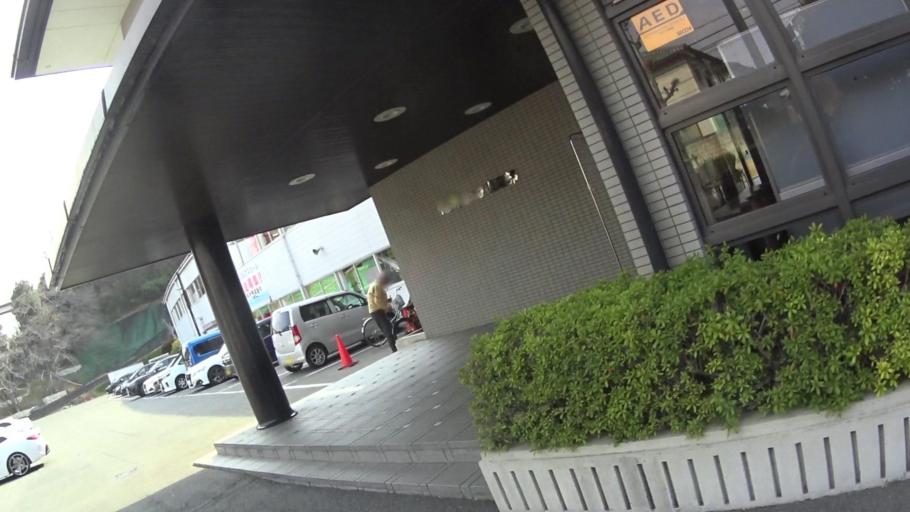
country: JP
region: Nara
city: Nara-shi
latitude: 34.7028
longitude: 135.8271
